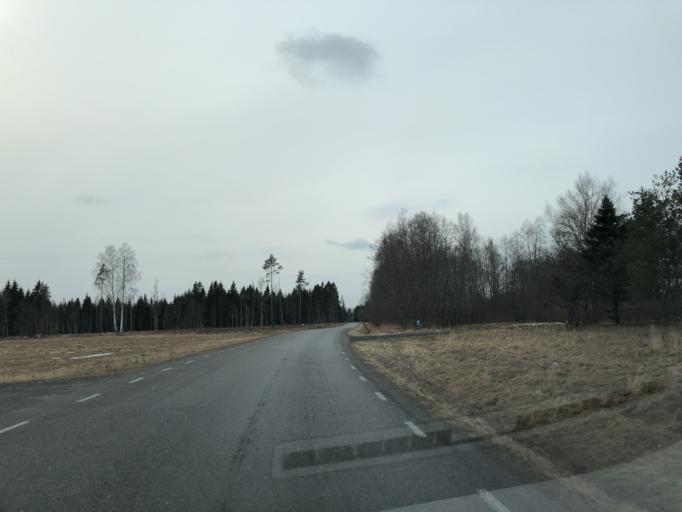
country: EE
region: Paernumaa
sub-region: Vaendra vald (alev)
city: Vandra
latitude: 58.6858
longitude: 24.9899
